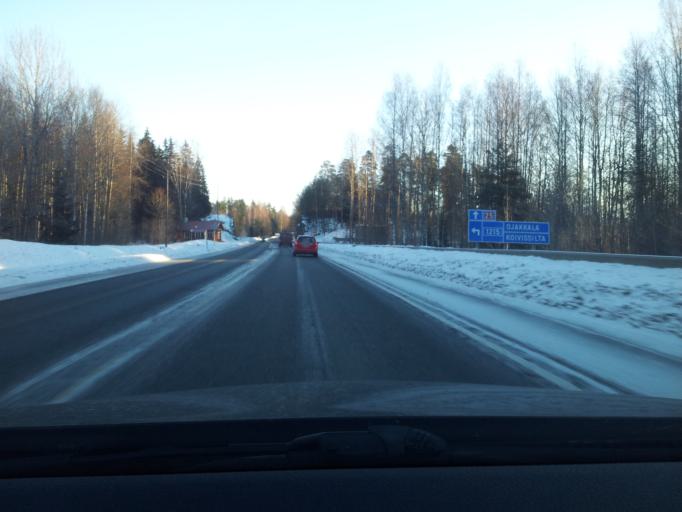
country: FI
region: Uusimaa
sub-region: Helsinki
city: Vihti
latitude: 60.3690
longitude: 24.3713
